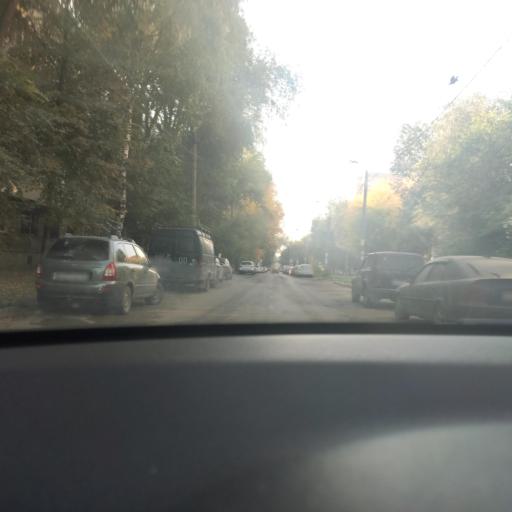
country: RU
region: Samara
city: Petra-Dubrava
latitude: 53.2385
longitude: 50.2842
